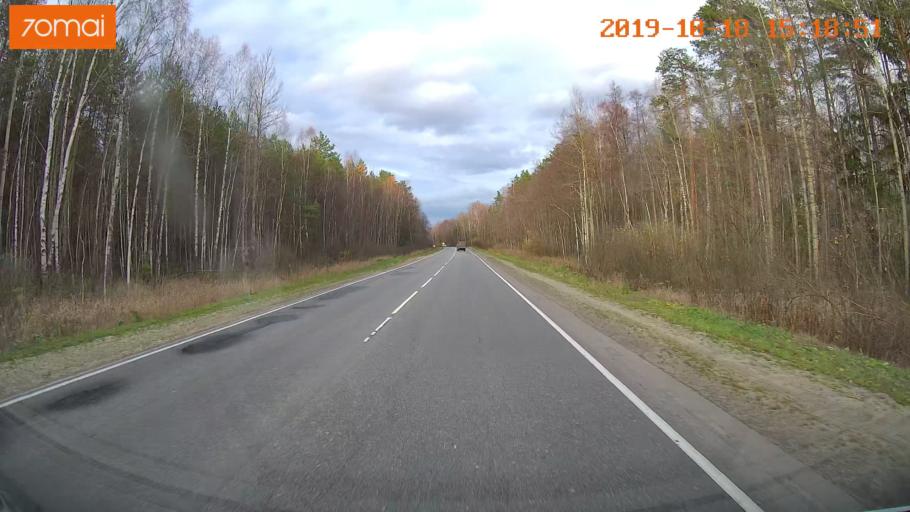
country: RU
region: Vladimir
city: Anopino
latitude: 55.6647
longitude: 40.7329
